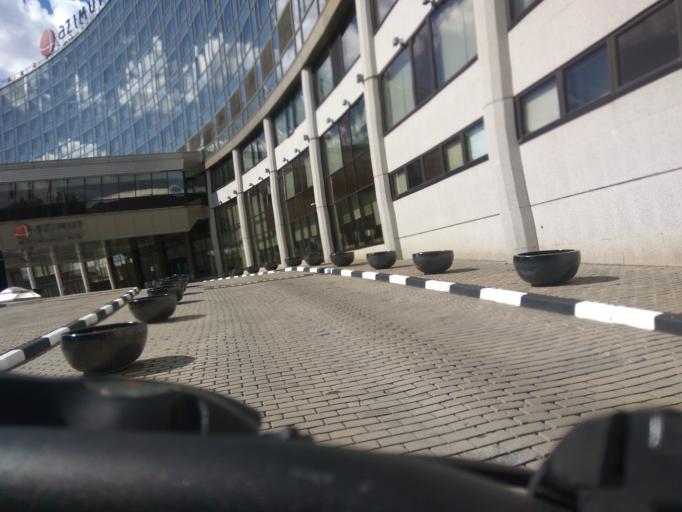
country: RU
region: Moscow
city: Mar'ina Roshcha
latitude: 55.7847
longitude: 37.6246
